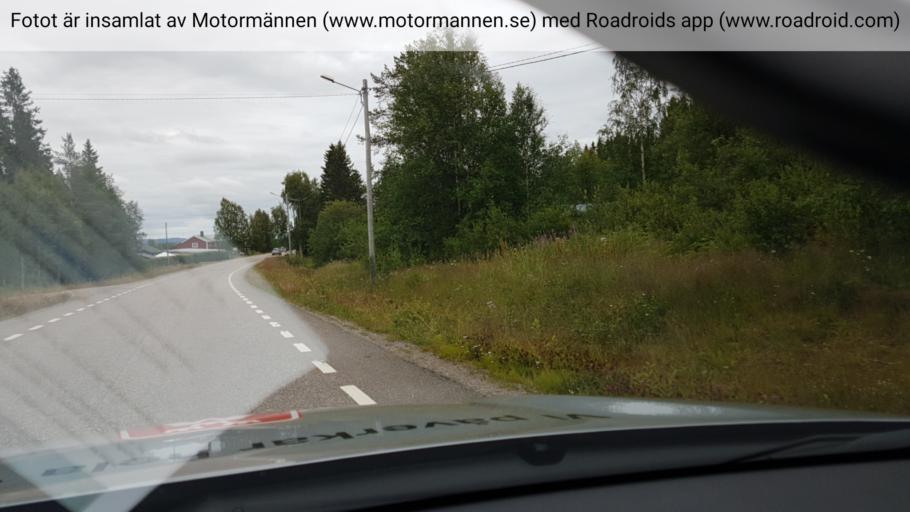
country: SE
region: Norrbotten
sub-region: Gallivare Kommun
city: Gaellivare
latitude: 67.0237
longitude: 21.8012
